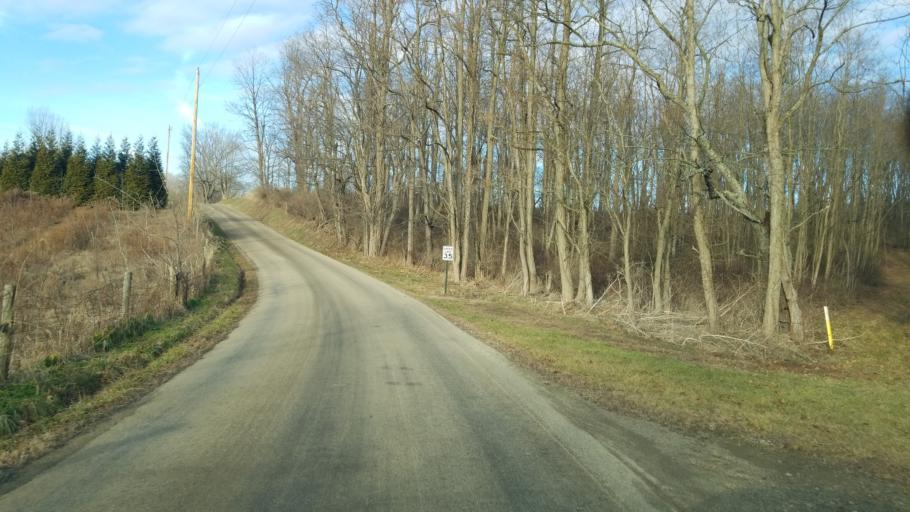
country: US
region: Ohio
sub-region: Knox County
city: Gambier
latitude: 40.3237
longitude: -82.3746
